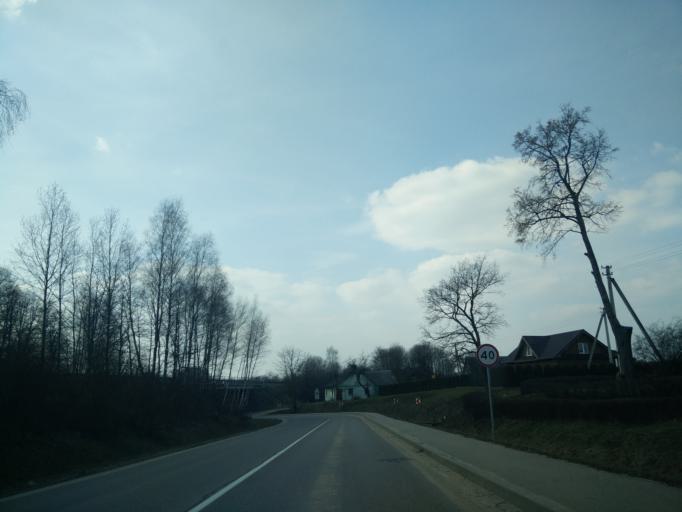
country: LT
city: Trakai
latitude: 54.6279
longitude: 24.9568
